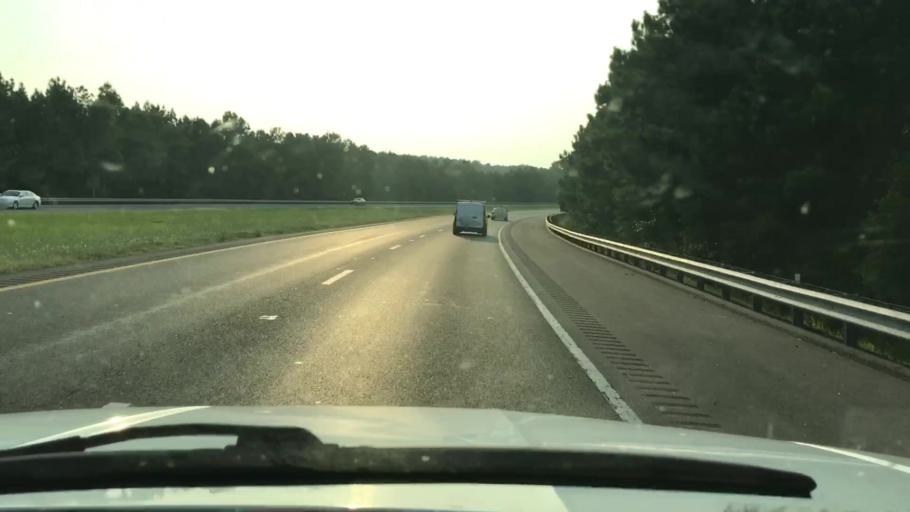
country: US
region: Virginia
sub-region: Chesterfield County
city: Brandermill
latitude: 37.4100
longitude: -77.6119
